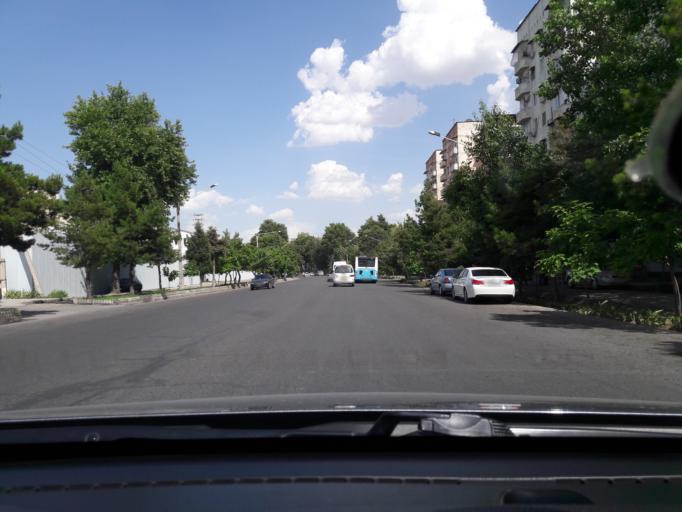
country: TJ
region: Dushanbe
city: Dushanbe
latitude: 38.5186
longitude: 68.7504
